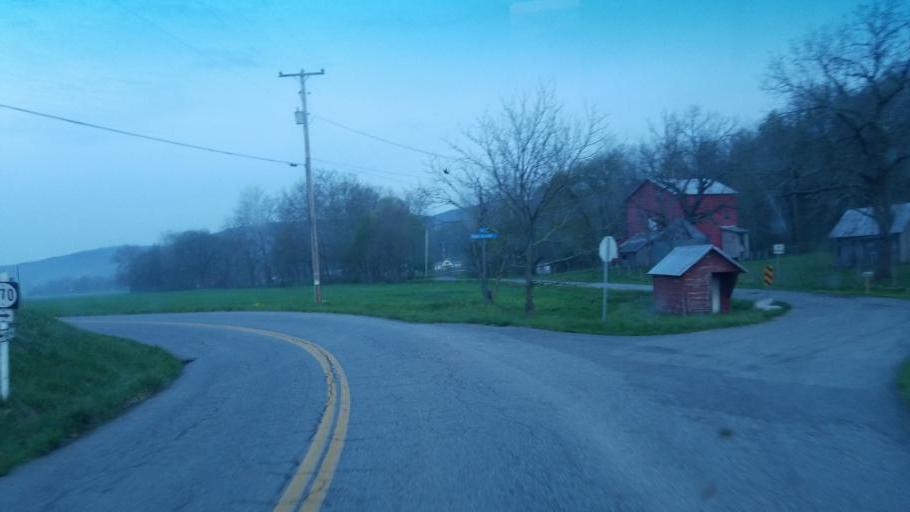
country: US
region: Virginia
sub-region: Smyth County
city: Atkins
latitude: 36.7735
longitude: -81.4360
